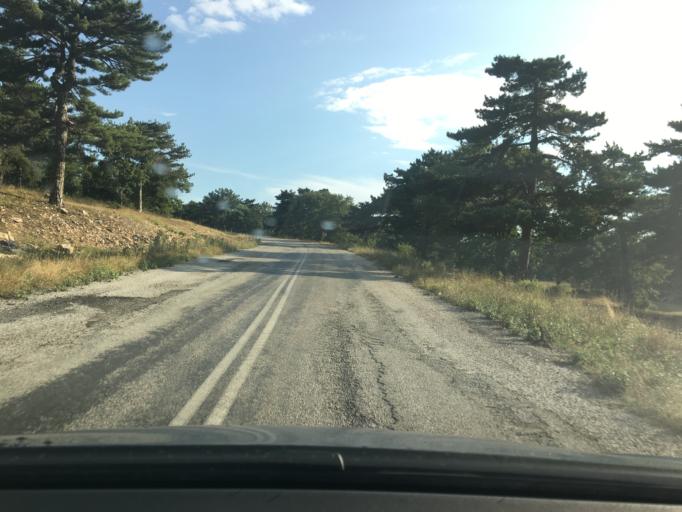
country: TR
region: Eskisehir
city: Seyitgazi
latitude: 39.3356
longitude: 30.6717
